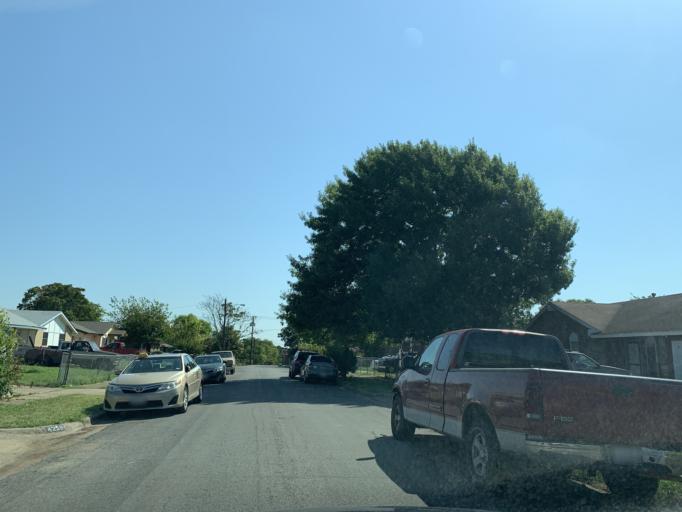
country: US
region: Texas
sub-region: Dallas County
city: Hutchins
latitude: 32.6673
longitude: -96.7452
